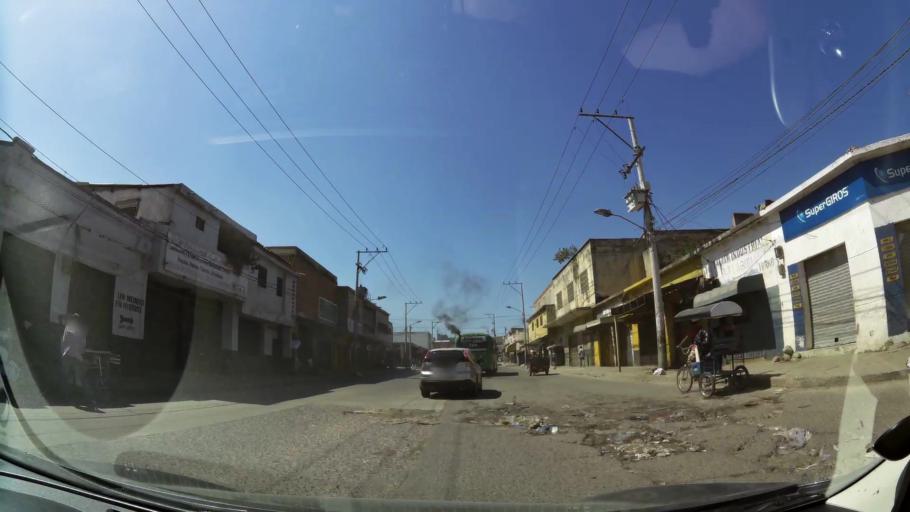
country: CO
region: Atlantico
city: Barranquilla
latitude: 10.9758
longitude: -74.7762
